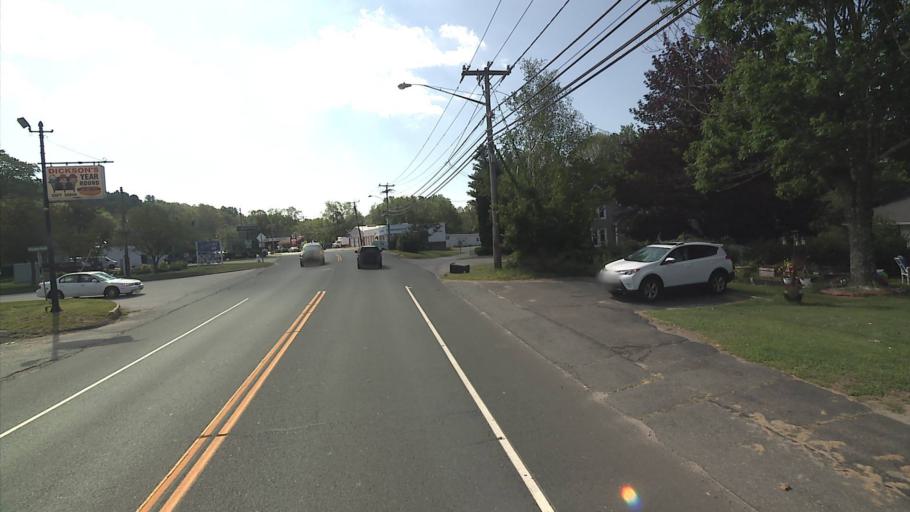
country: US
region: Connecticut
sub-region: Tolland County
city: Stafford Springs
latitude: 41.9608
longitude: -72.3146
